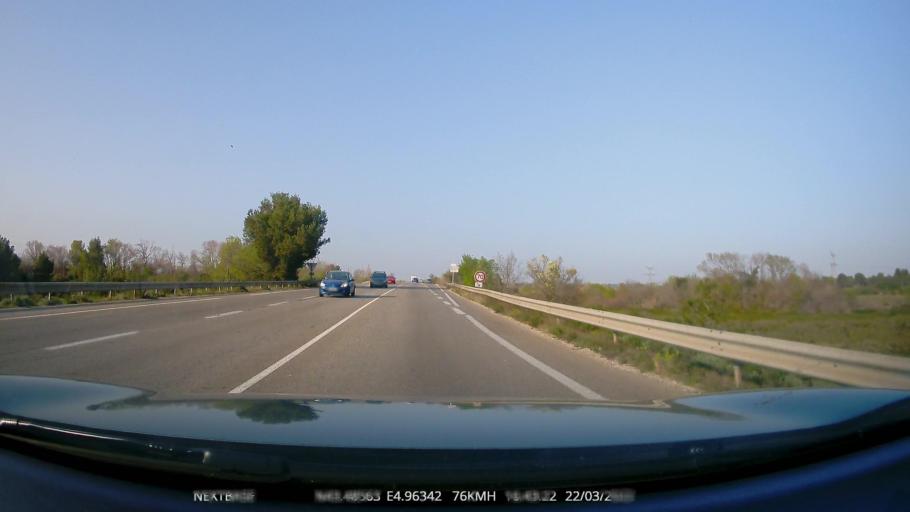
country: FR
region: Provence-Alpes-Cote d'Azur
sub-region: Departement des Bouches-du-Rhone
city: Istres
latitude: 43.4857
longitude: 4.9633
